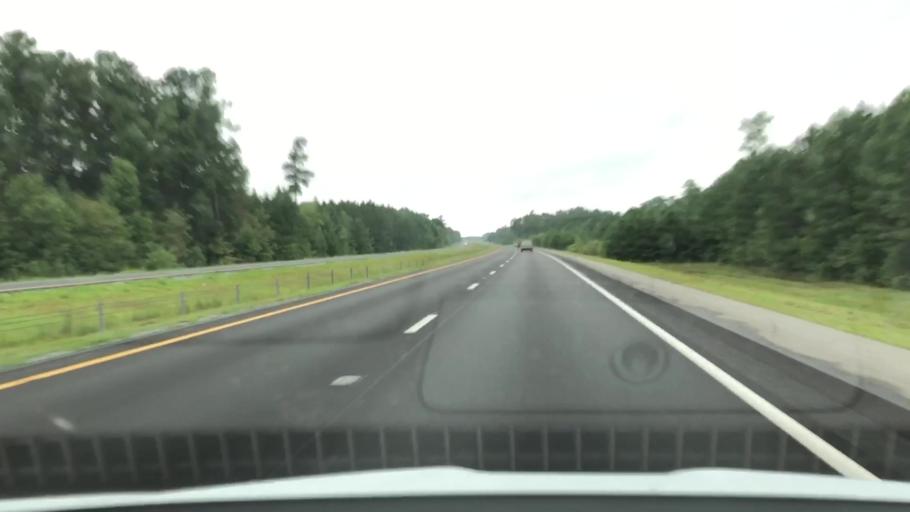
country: US
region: North Carolina
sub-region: Wayne County
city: Goldsboro
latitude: 35.4503
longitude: -77.9843
